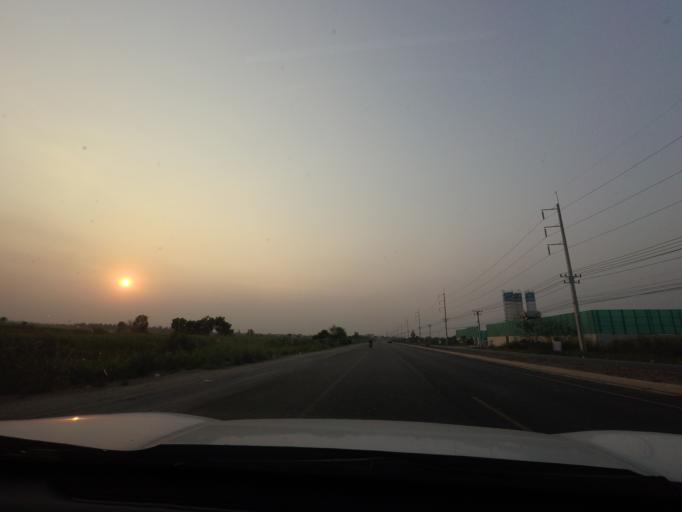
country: TH
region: Nakhon Nayok
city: Ongkharak
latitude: 14.1144
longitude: 101.0135
